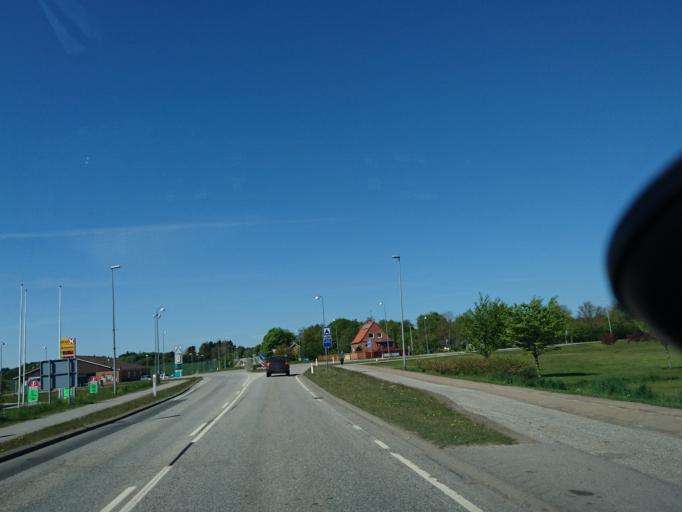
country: DK
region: North Denmark
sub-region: Hjorring Kommune
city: Sindal
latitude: 57.4707
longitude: 10.1985
